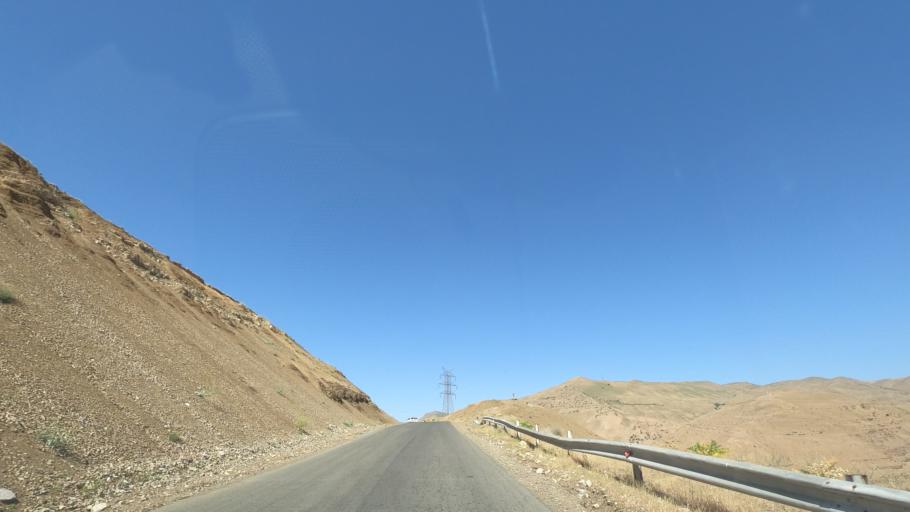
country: IR
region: Alborz
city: Karaj
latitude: 35.9408
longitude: 51.0809
